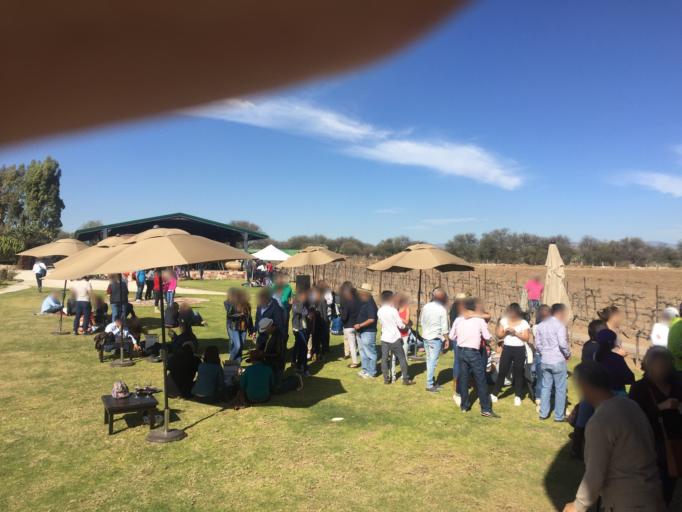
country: MX
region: Queretaro
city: Ezequiel Montes
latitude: 20.6373
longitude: -99.9000
